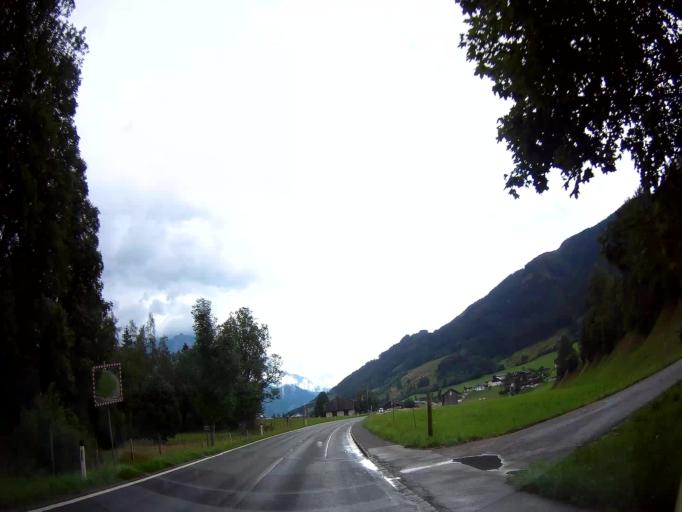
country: AT
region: Salzburg
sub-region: Politischer Bezirk Zell am See
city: Leogang
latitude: 47.4403
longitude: 12.7679
